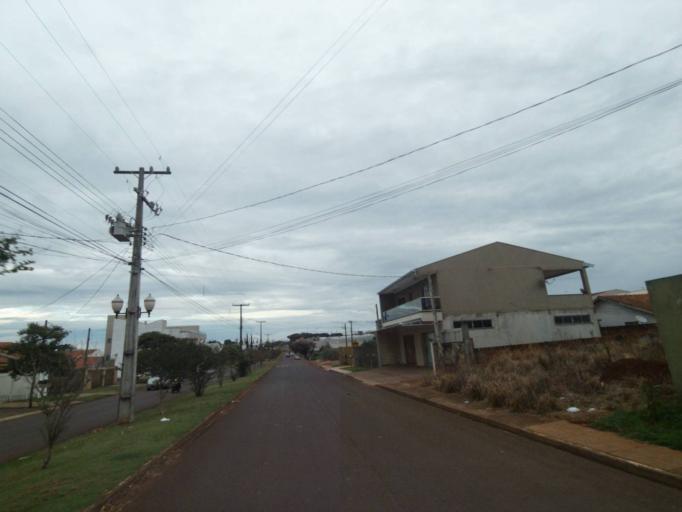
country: BR
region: Parana
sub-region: Campo Mourao
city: Campo Mourao
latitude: -24.0299
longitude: -52.3589
